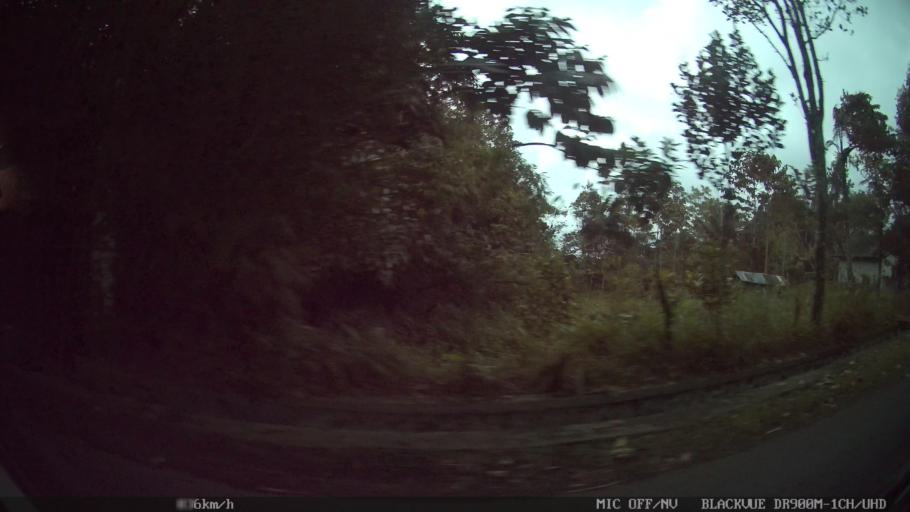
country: ID
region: Bali
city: Banjar Bias
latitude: -8.3726
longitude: 115.4328
